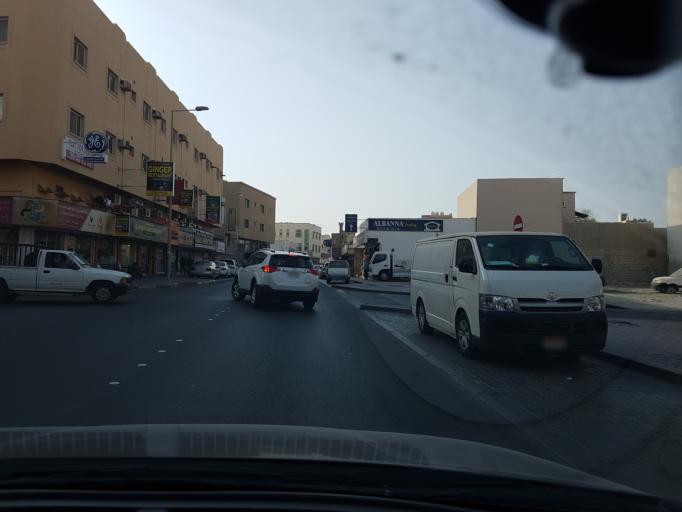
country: BH
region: Northern
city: Ar Rifa'
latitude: 26.1179
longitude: 50.5694
